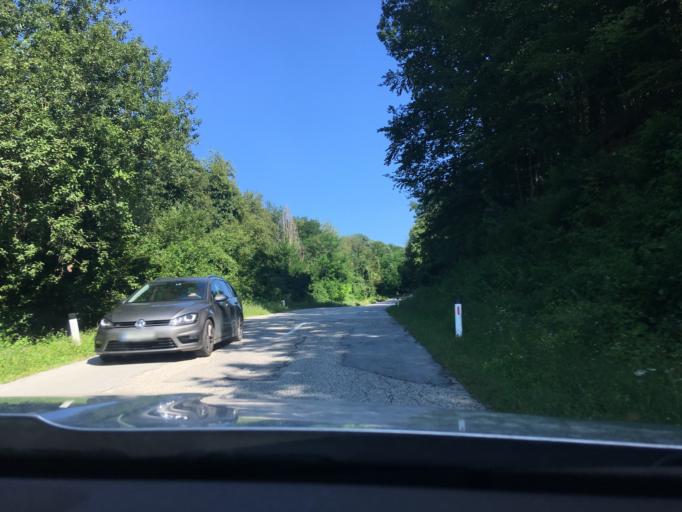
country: HR
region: Karlovacka
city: Ozalj
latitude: 45.4955
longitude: 15.3569
